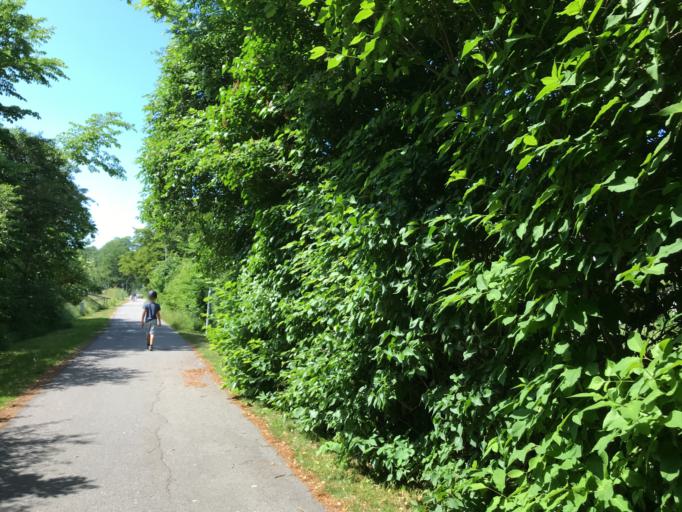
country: SE
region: Vaestra Goetaland
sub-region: Goteborg
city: Billdal
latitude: 57.5770
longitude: 11.9482
